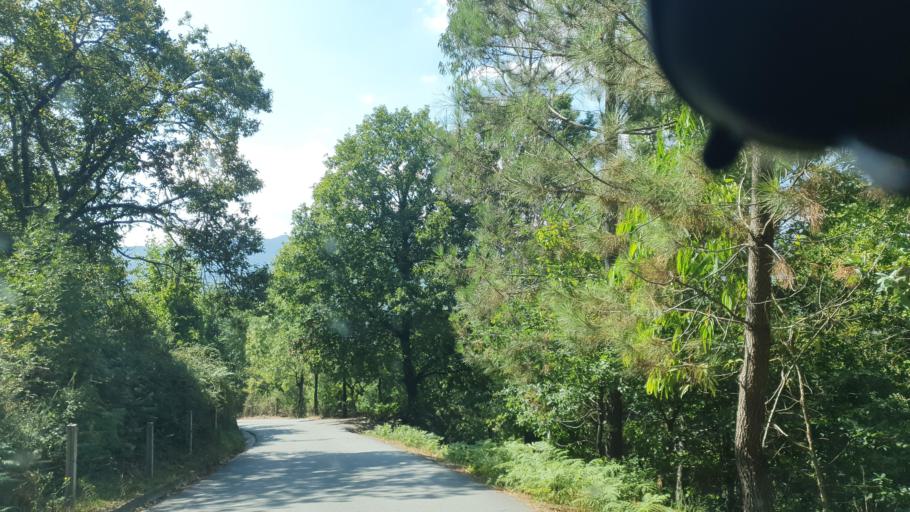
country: PT
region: Braga
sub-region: Vieira do Minho
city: Real
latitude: 41.6746
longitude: -8.1600
